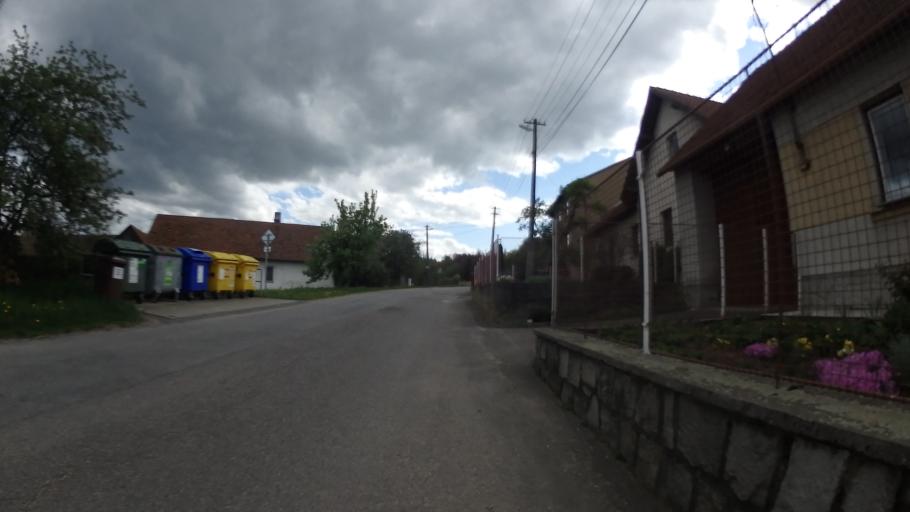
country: CZ
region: Vysocina
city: Merin
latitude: 49.3660
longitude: 15.8822
